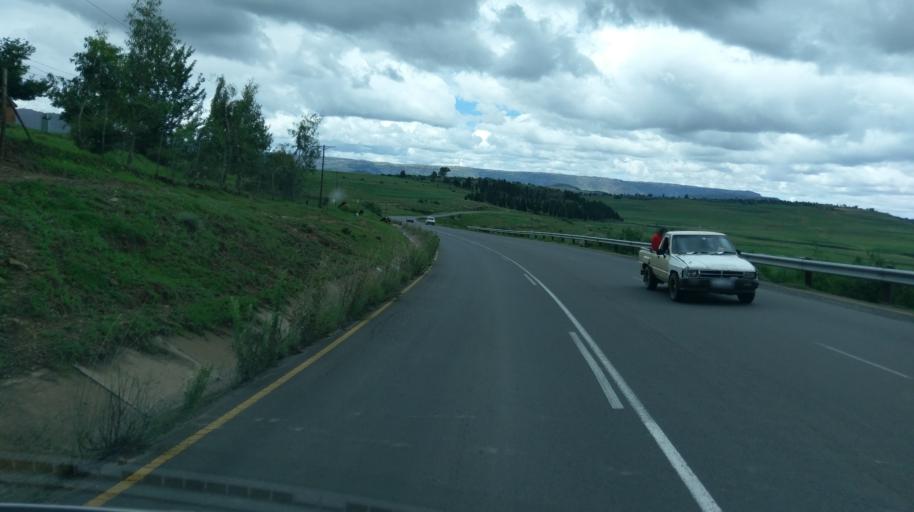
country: LS
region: Maseru
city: Maseru
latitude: -29.5109
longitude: 27.5227
